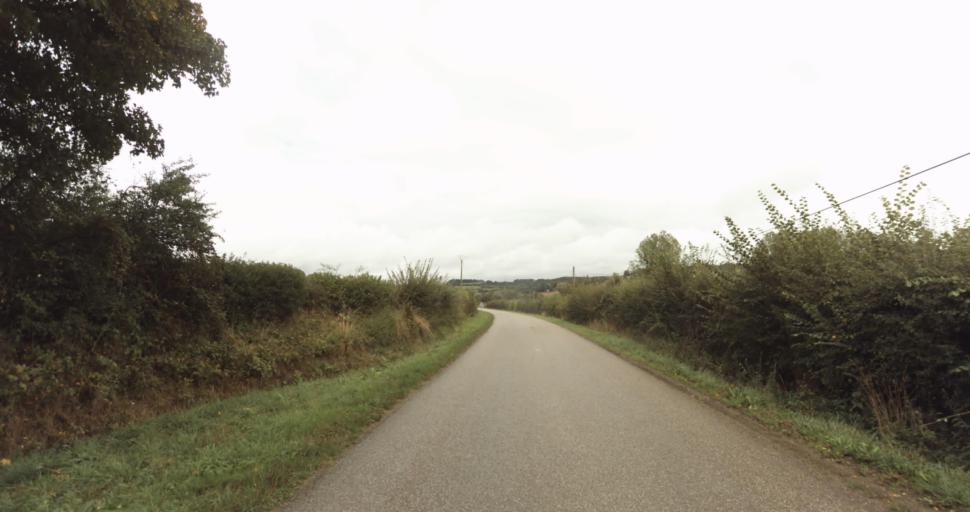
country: FR
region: Lower Normandy
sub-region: Departement de l'Orne
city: Vimoutiers
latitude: 48.8550
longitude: 0.2166
